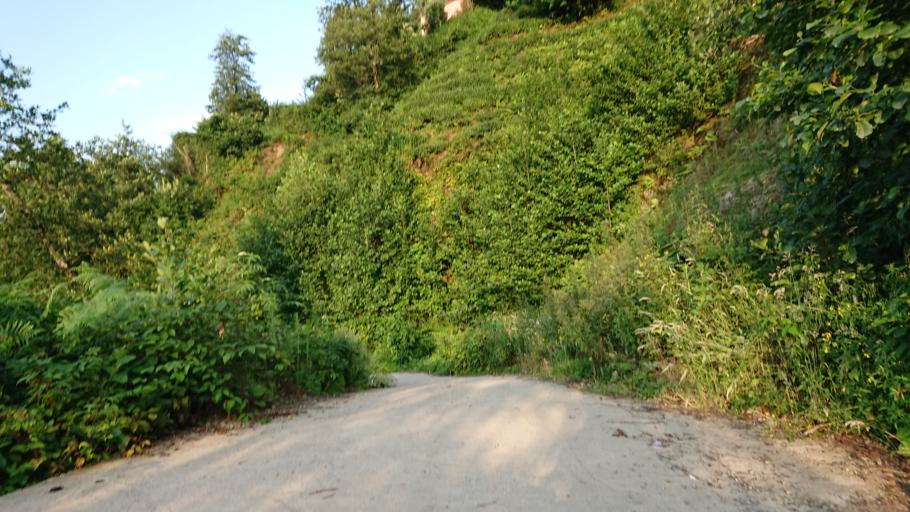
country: TR
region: Rize
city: Rize
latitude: 40.9923
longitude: 40.5035
